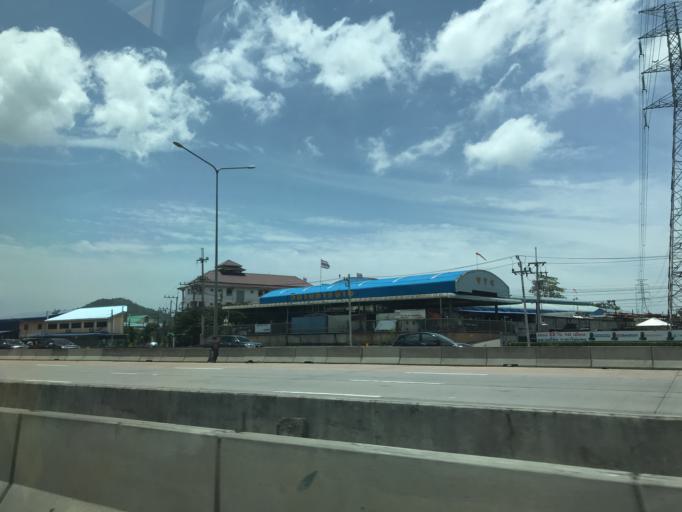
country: TH
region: Chon Buri
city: Si Racha
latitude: 13.1103
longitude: 100.9397
